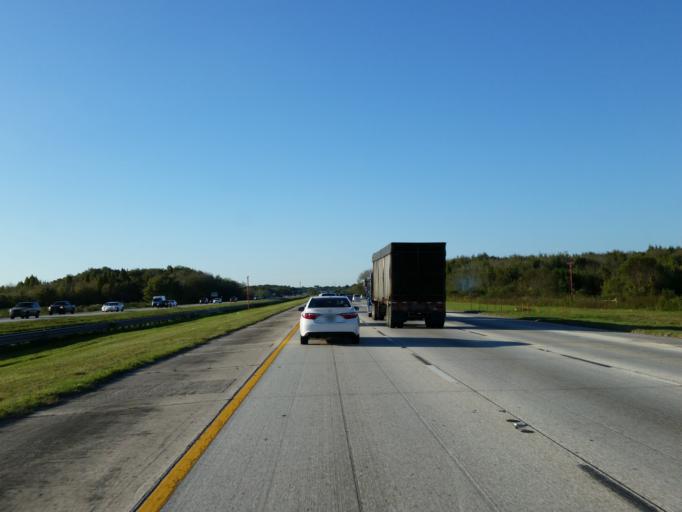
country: US
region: Florida
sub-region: Hillsborough County
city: Thonotosassa
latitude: 28.0225
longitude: -82.3352
